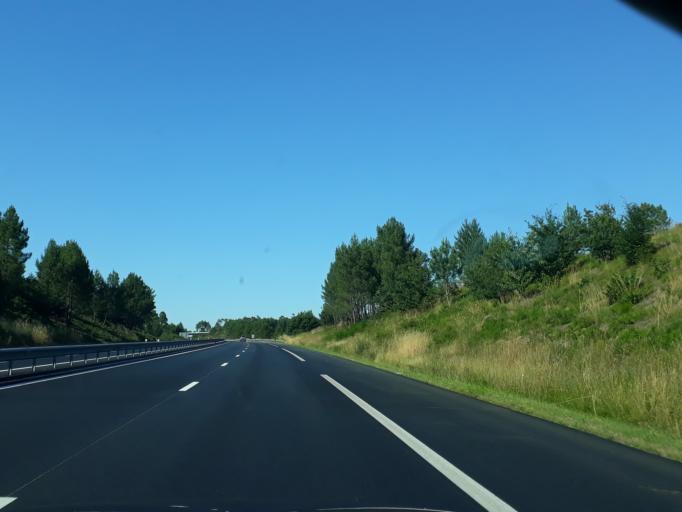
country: FR
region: Aquitaine
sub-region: Departement de la Dordogne
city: Sourzac
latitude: 45.0268
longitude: 0.3958
